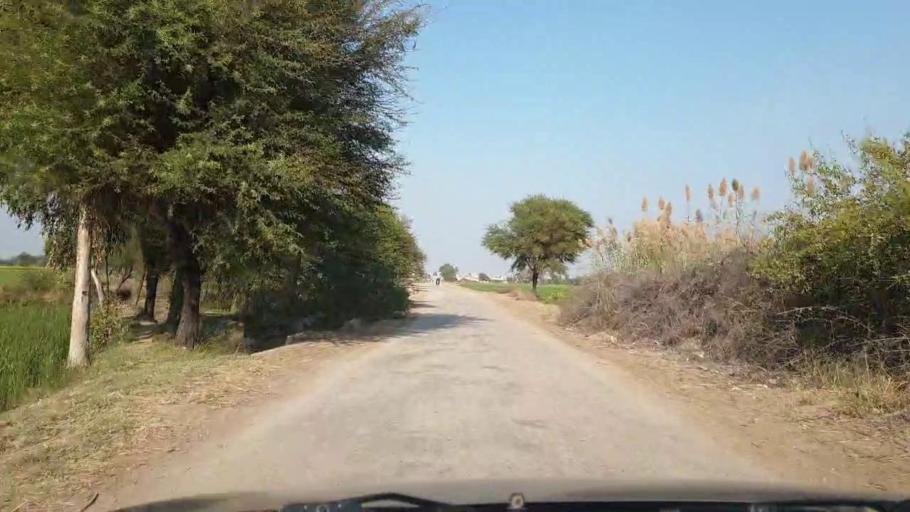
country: PK
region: Sindh
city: Jhol
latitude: 25.9442
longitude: 68.8834
